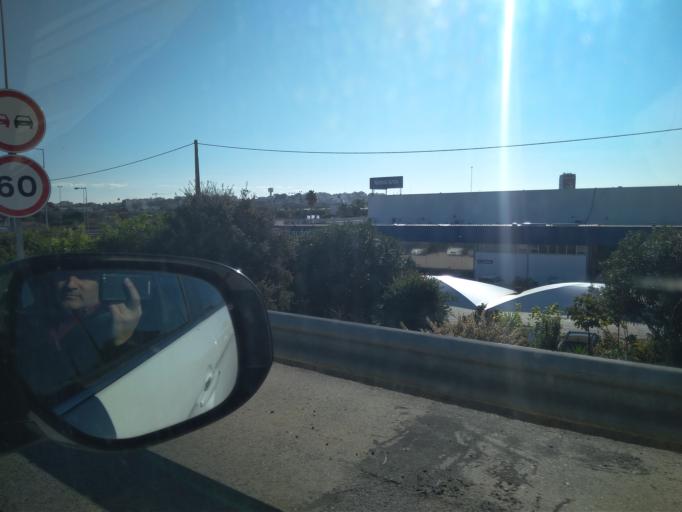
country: PT
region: Faro
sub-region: Faro
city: Faro
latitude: 37.0385
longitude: -7.9517
